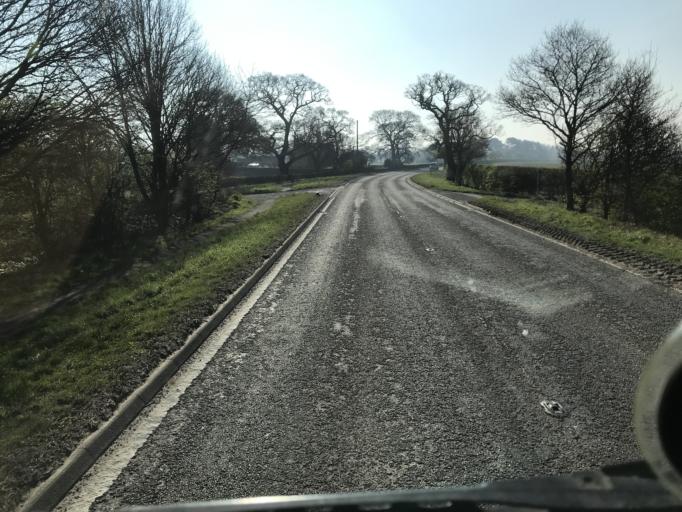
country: GB
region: England
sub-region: Cheshire West and Chester
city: Waverton
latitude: 53.1612
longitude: -2.8155
